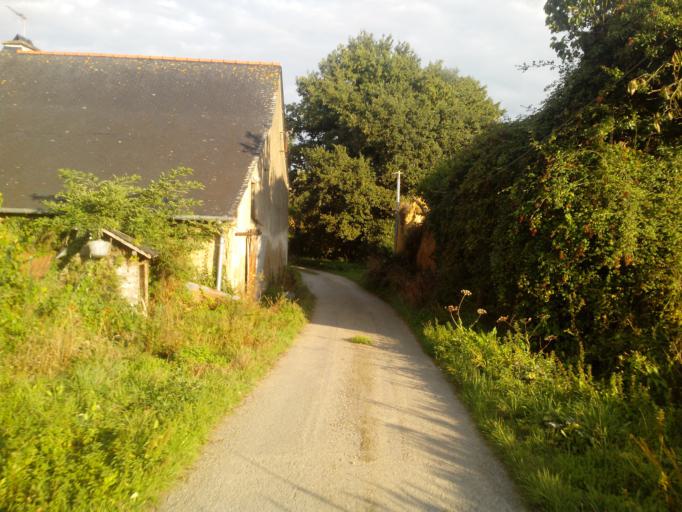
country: FR
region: Brittany
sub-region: Departement d'Ille-et-Vilaine
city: Brece
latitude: 48.1301
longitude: -1.4902
